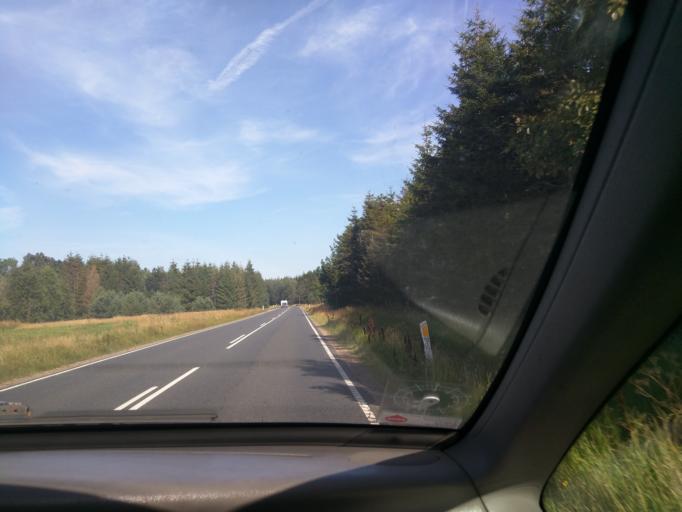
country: DK
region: Central Jutland
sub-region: Viborg Kommune
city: Bjerringbro
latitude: 56.2969
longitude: 9.6764
